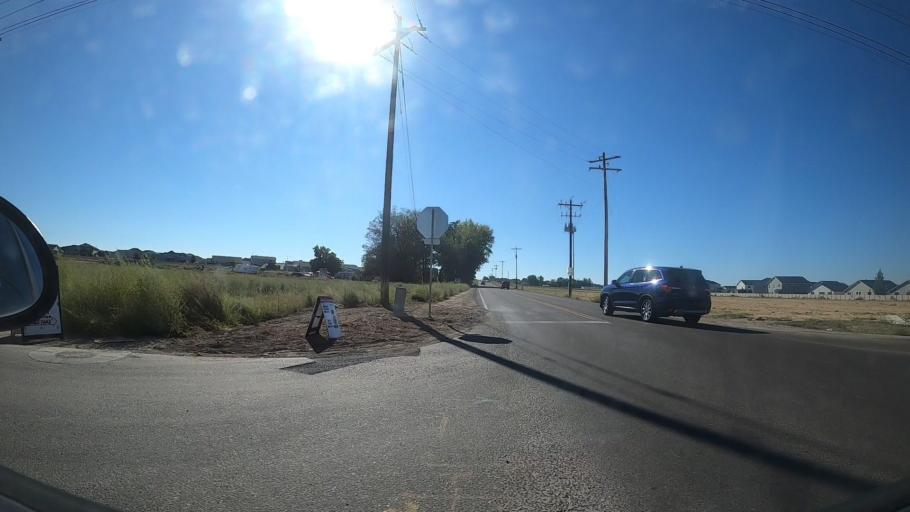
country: US
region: Idaho
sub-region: Canyon County
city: Nampa
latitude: 43.5619
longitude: -116.6130
